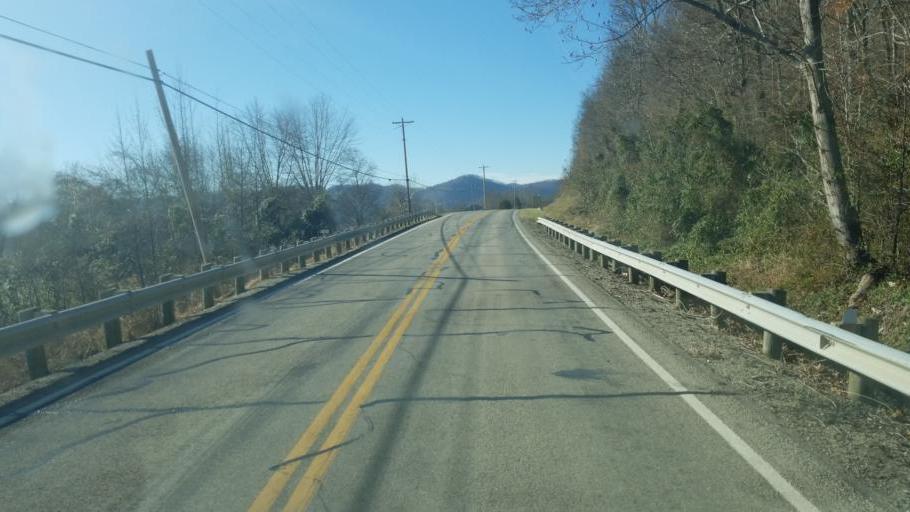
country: US
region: Kentucky
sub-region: Lewis County
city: Vanceburg
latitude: 38.6246
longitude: -83.1675
